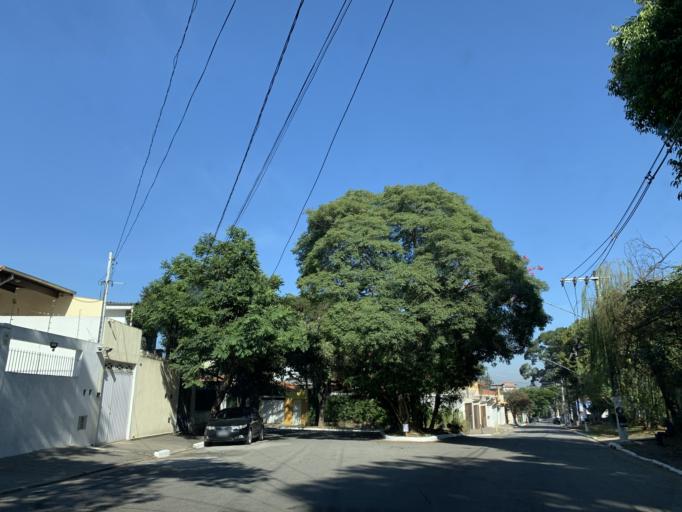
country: BR
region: Sao Paulo
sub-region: Diadema
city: Diadema
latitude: -23.6732
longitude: -46.6878
